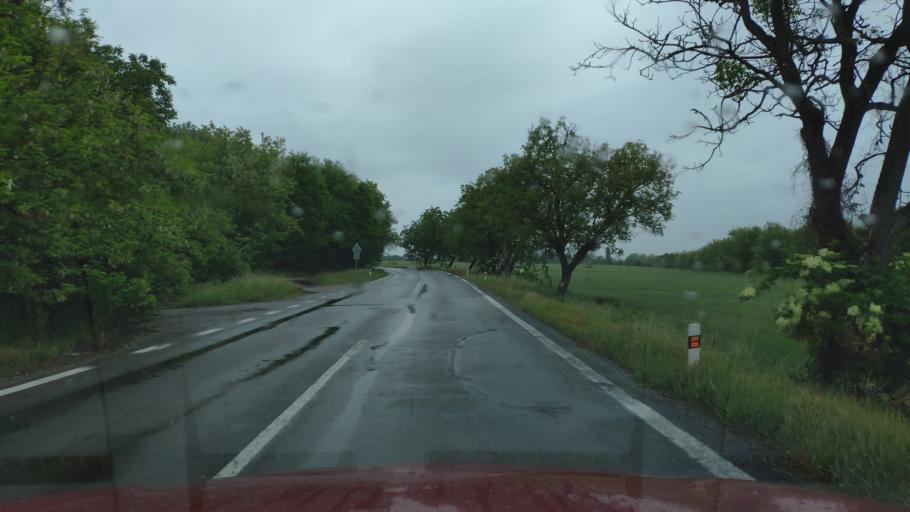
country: HU
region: Borsod-Abauj-Zemplen
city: Karcsa
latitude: 48.3898
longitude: 21.7906
